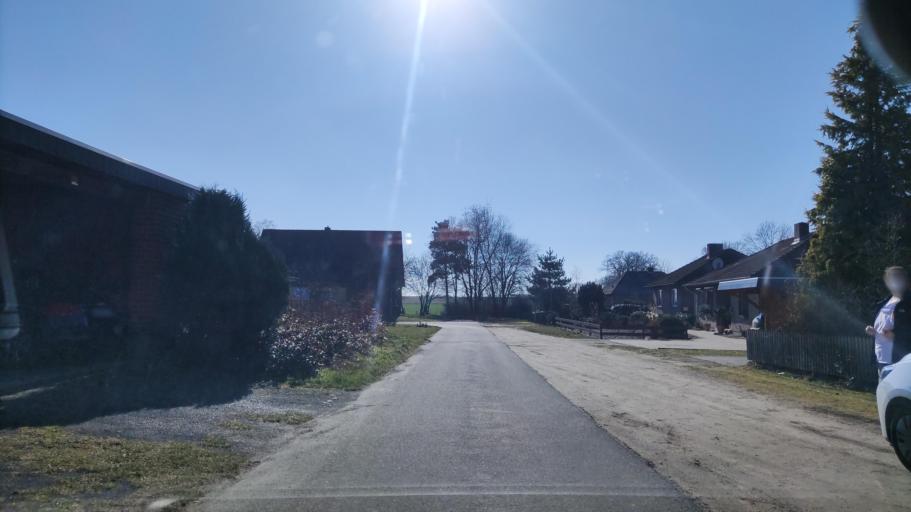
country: DE
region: Lower Saxony
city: Jelmstorf
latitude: 53.1025
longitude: 10.5168
